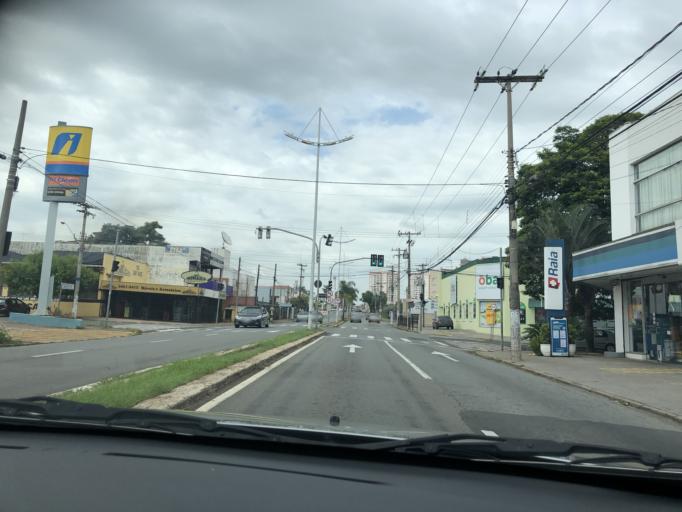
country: BR
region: Sao Paulo
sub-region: Americana
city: Americana
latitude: -22.7583
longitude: -47.3386
